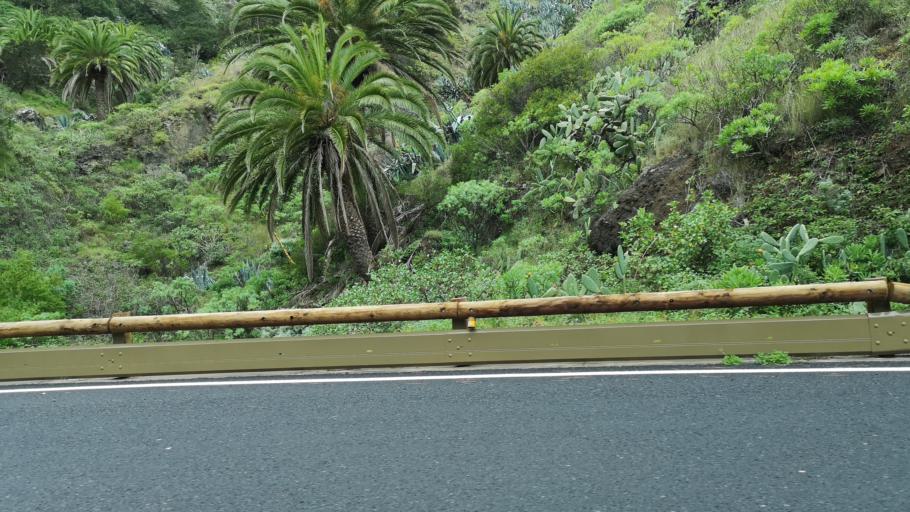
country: ES
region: Canary Islands
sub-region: Provincia de Santa Cruz de Tenerife
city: Hermigua
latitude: 28.1436
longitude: -17.2005
